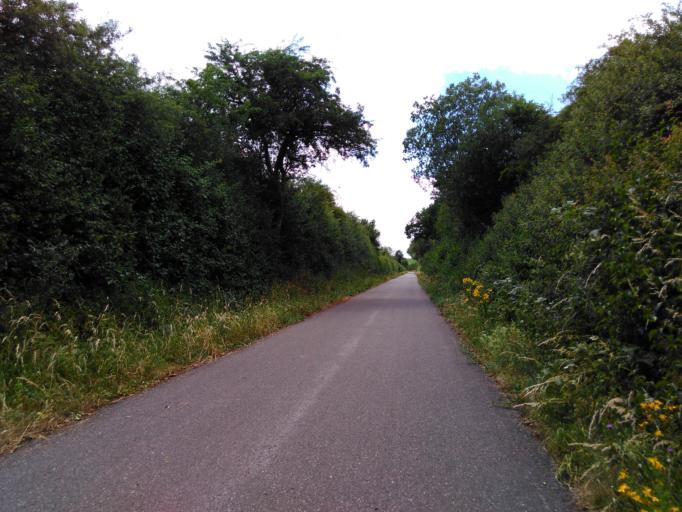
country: LU
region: Luxembourg
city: Hautcharage
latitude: 49.5941
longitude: 5.9014
